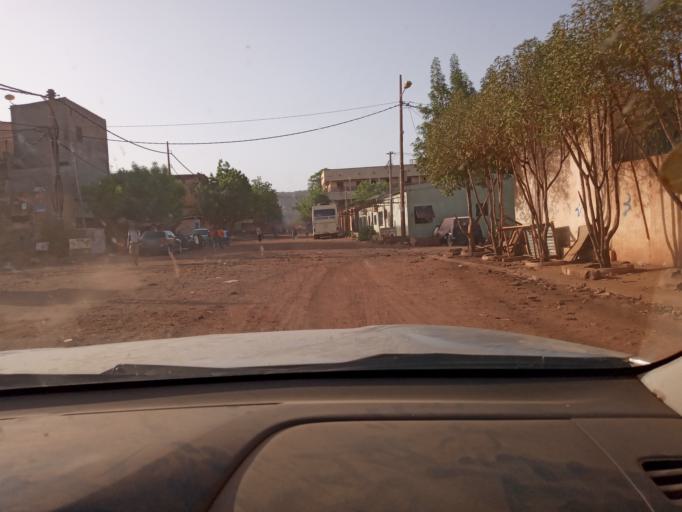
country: ML
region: Bamako
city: Bamako
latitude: 12.6673
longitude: -7.9744
